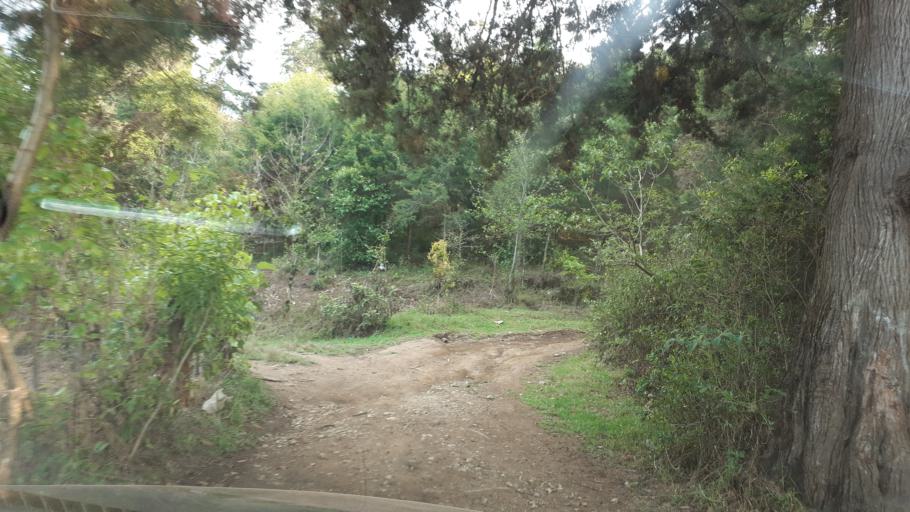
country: GT
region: Chimaltenango
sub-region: Municipio de Chimaltenango
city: Chimaltenango
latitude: 14.6516
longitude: -90.8453
